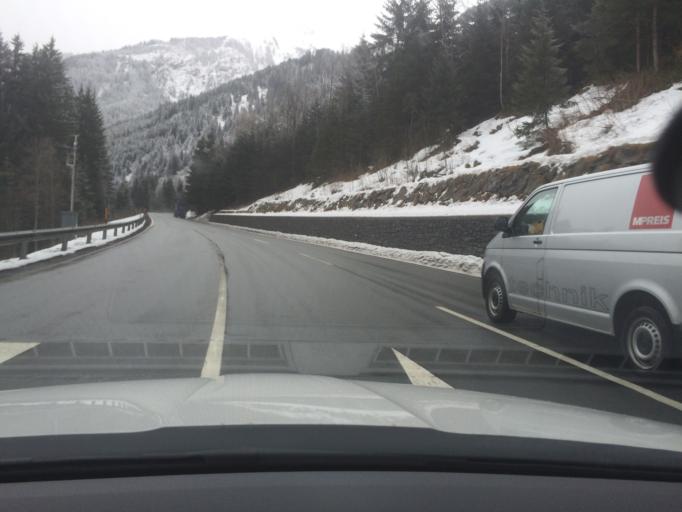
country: AT
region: Salzburg
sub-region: Politischer Bezirk Zell am See
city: Mittersill
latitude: 47.2215
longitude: 12.4878
